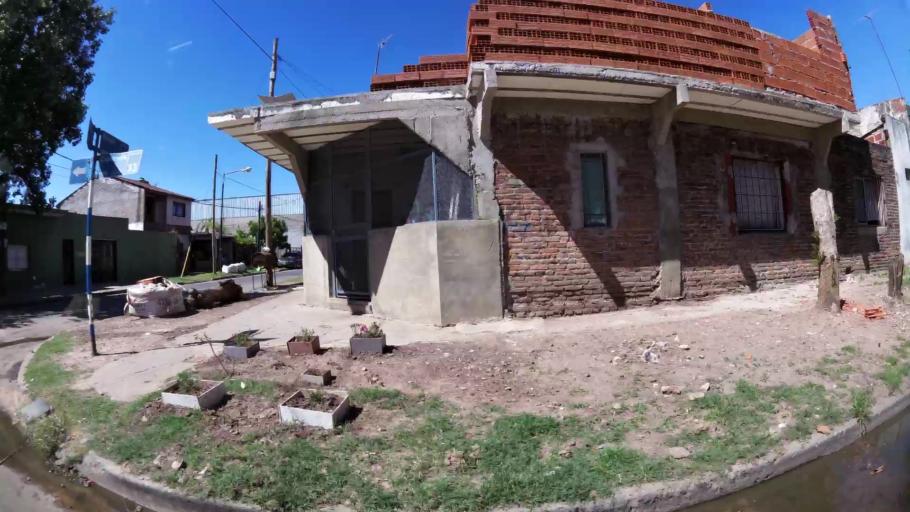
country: AR
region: Buenos Aires
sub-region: Partido de General San Martin
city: General San Martin
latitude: -34.5262
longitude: -58.5650
